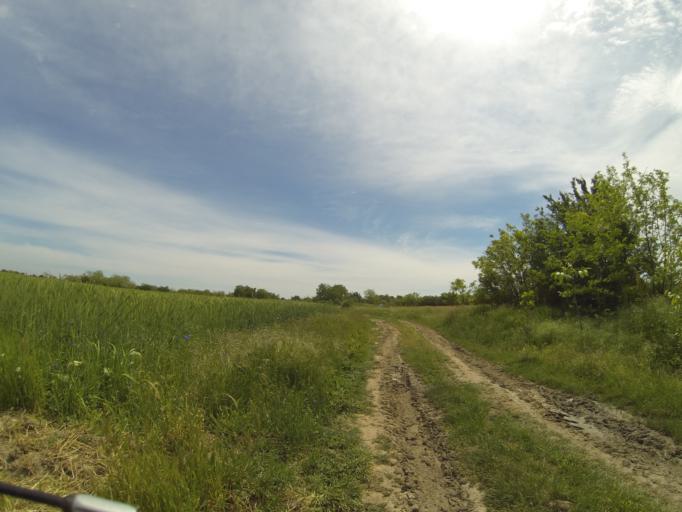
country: RO
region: Dolj
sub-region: Comuna Leu
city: Leu
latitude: 44.1980
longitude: 23.9910
